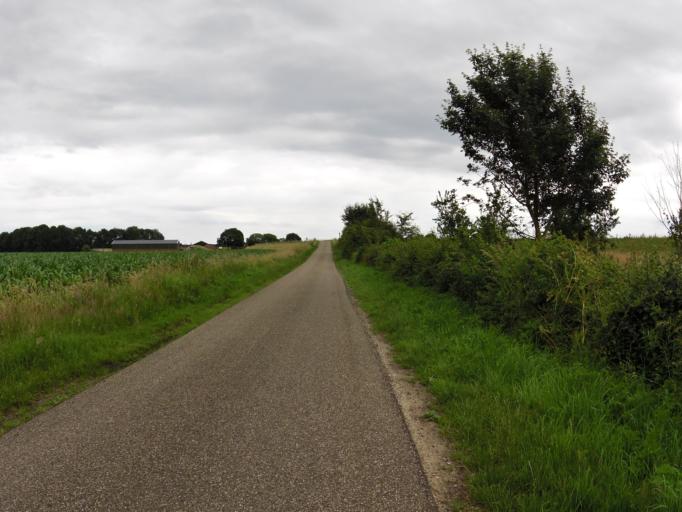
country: NL
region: North Brabant
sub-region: Gemeente Landerd
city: Reek
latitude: 51.7681
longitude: 5.6893
